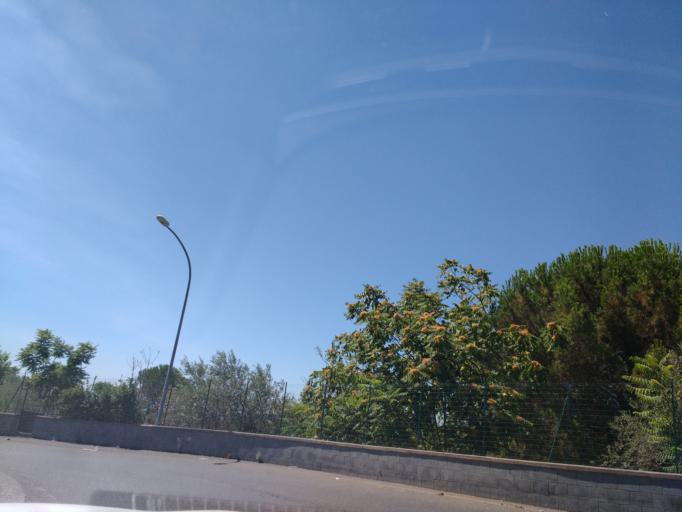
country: IT
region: Sicily
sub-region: Catania
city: Nicolosi
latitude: 37.6090
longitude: 15.0307
